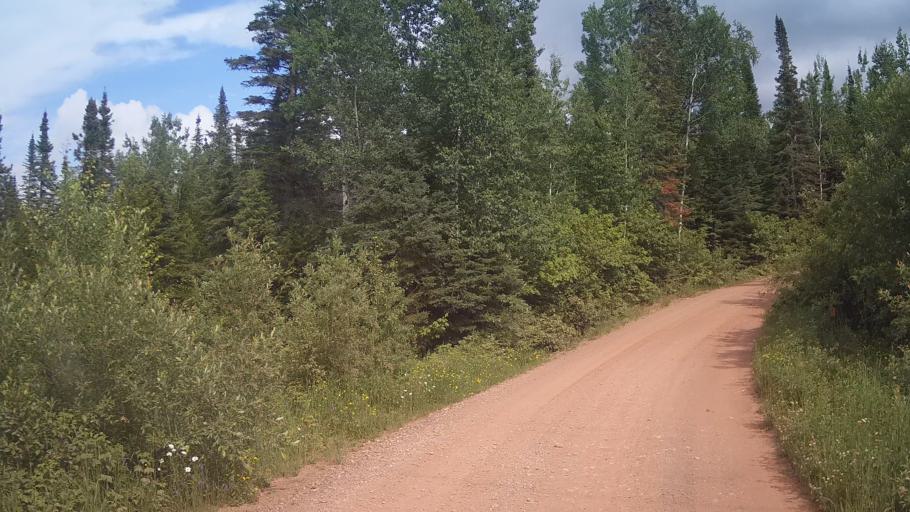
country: CA
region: Ontario
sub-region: Thunder Bay District
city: Thunder Bay
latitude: 48.6705
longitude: -88.6663
